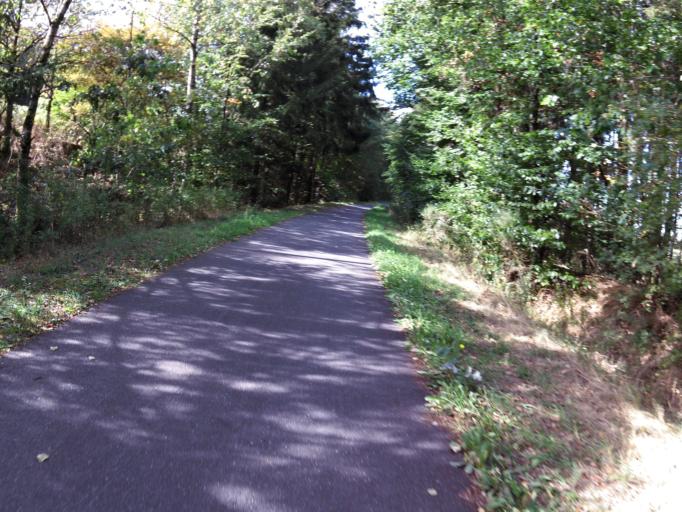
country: DE
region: Rheinland-Pfalz
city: Bleialf
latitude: 50.2184
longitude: 6.2709
